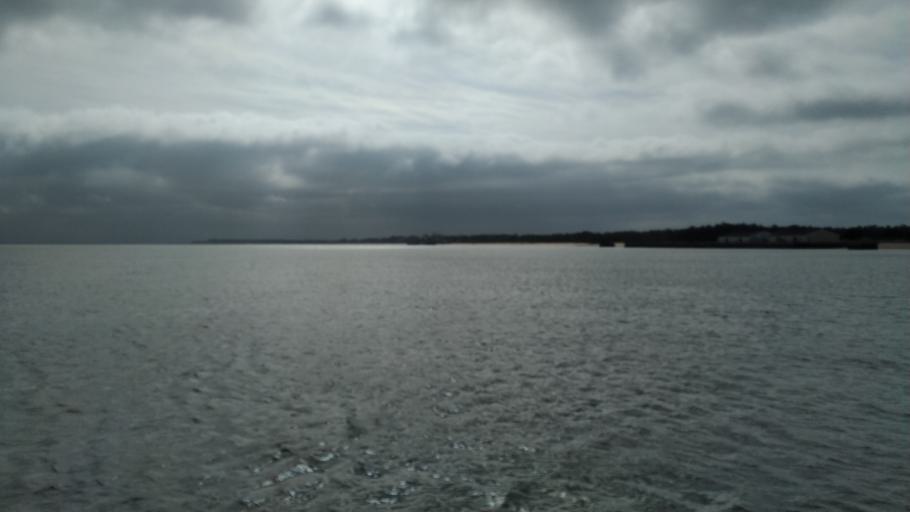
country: PT
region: Setubal
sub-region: Setubal
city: Setubal
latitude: 38.4807
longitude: -8.8709
